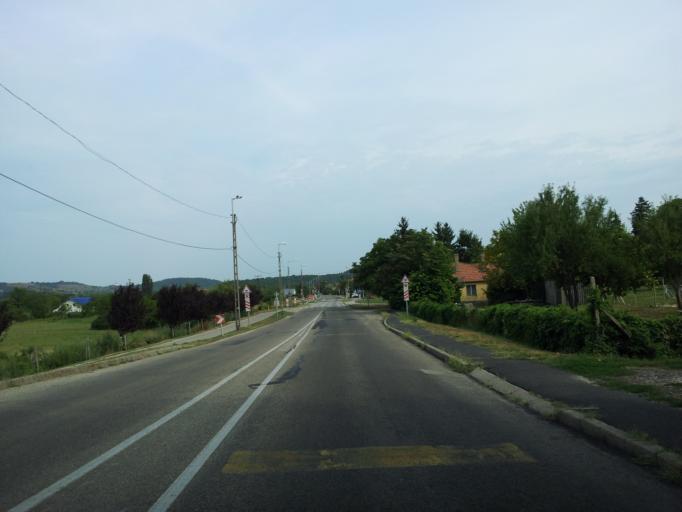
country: HU
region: Veszprem
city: Balatonfured
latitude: 46.9275
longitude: 17.8355
